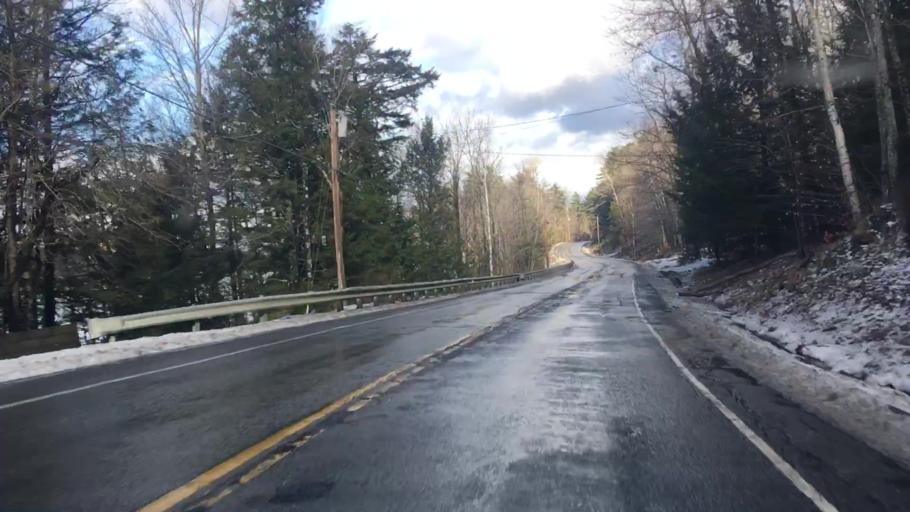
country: US
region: Maine
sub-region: Hancock County
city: Dedham
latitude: 44.6546
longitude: -68.6825
